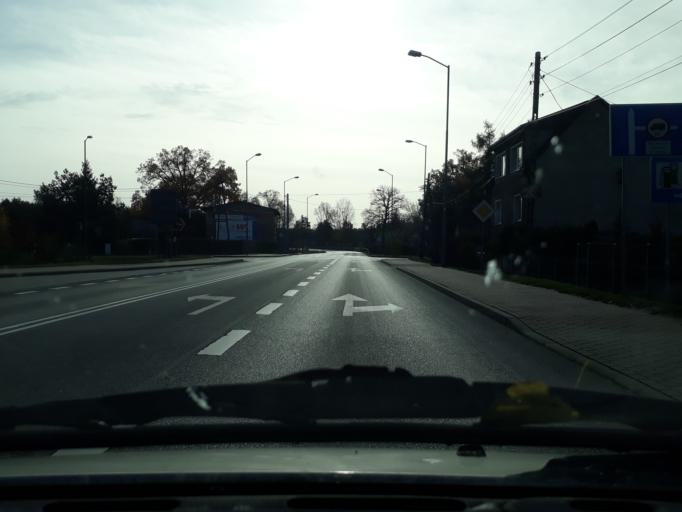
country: PL
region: Silesian Voivodeship
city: Miasteczko Slaskie
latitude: 50.5510
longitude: 18.9558
